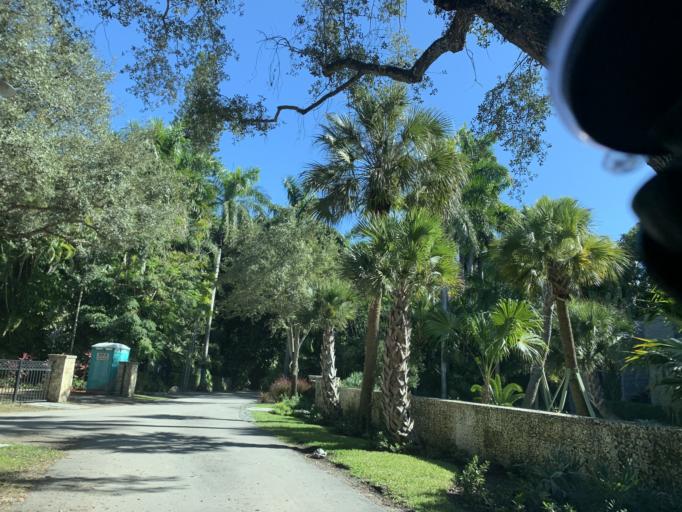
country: US
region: Florida
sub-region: Miami-Dade County
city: Coconut Grove
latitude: 25.7187
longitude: -80.2567
